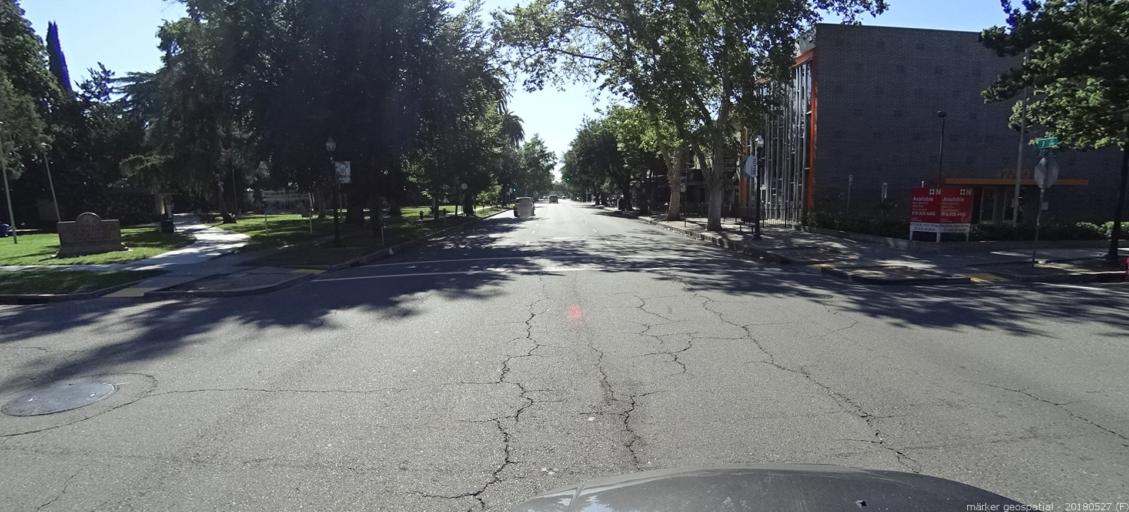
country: US
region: California
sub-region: Sacramento County
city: Sacramento
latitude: 38.5743
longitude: -121.4707
